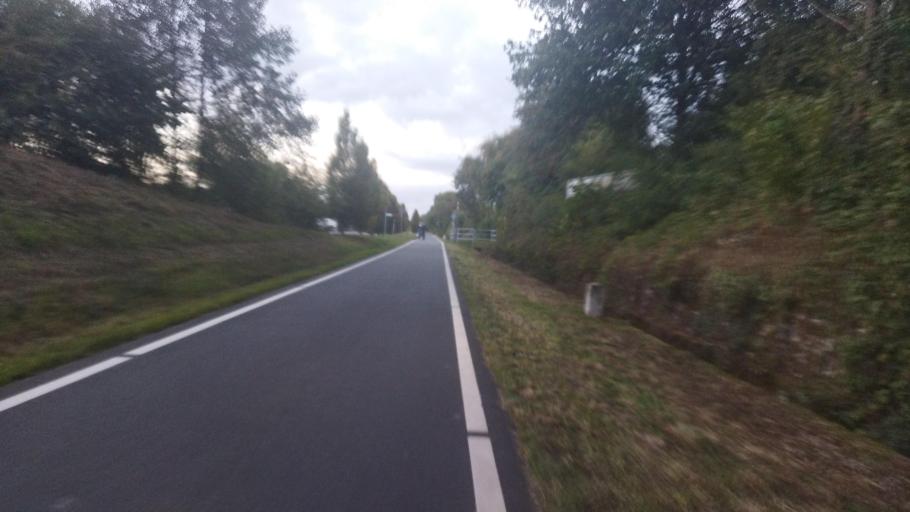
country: DE
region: North Rhine-Westphalia
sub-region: Regierungsbezirk Munster
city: Horstmar
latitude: 52.0626
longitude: 7.3206
